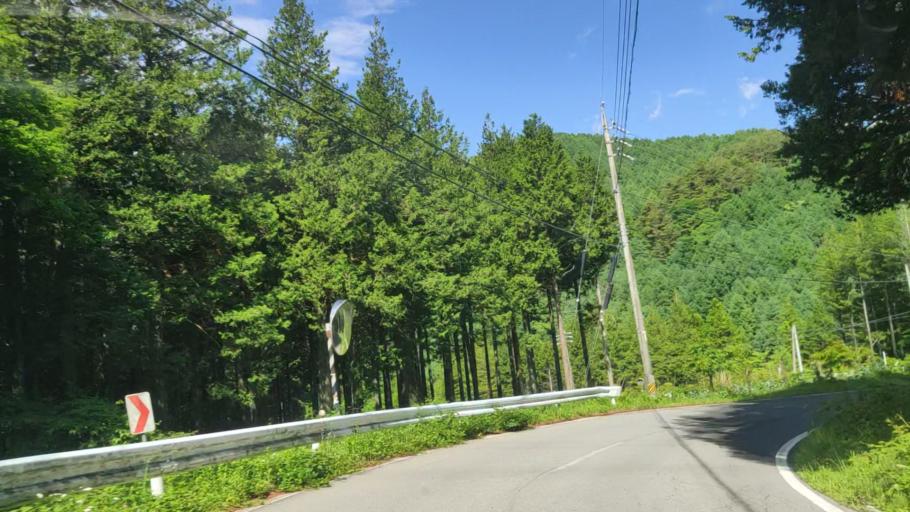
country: JP
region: Nagano
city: Suwa
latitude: 36.0750
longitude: 138.1385
